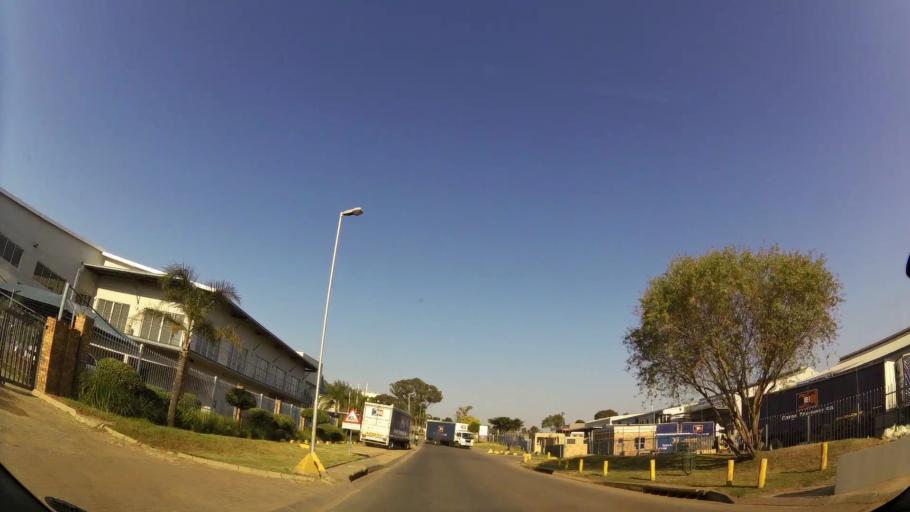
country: ZA
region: Gauteng
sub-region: City of Johannesburg Metropolitan Municipality
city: Modderfontein
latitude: -26.1512
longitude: 28.1759
